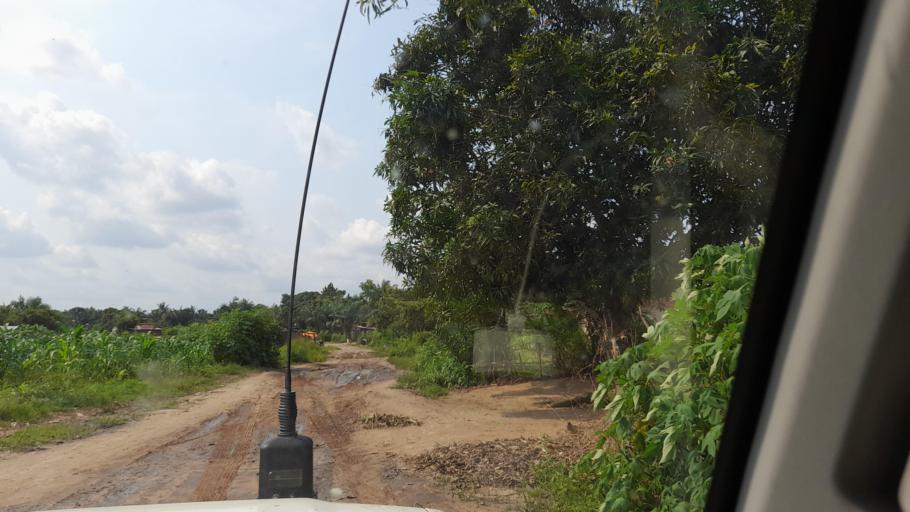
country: CD
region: Kasai-Occidental
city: Kananga
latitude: -5.9073
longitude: 22.4755
